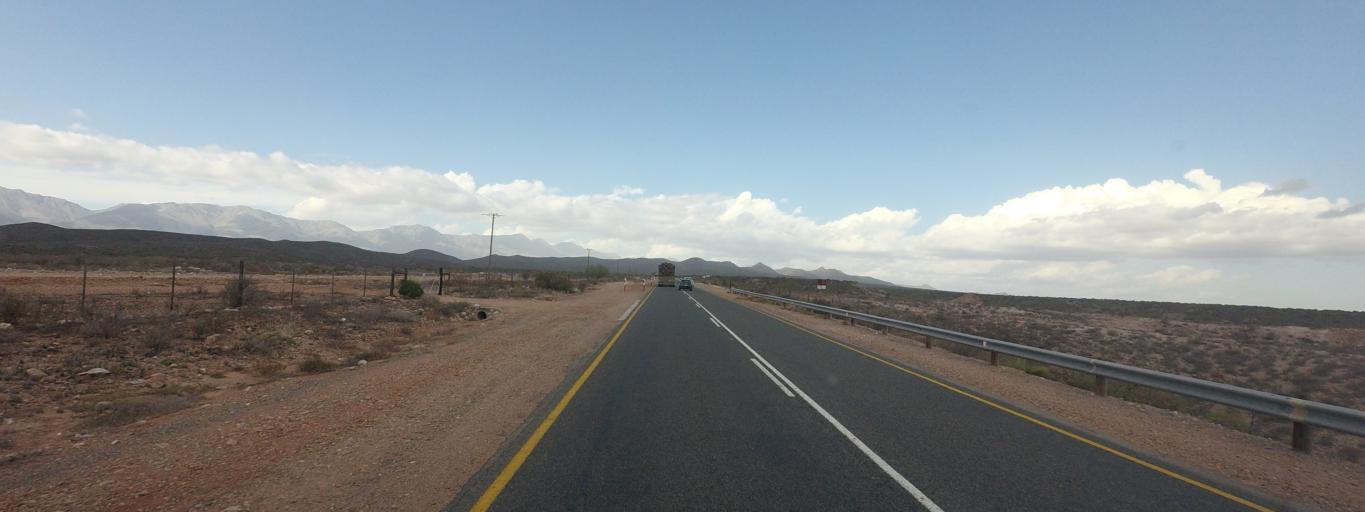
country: ZA
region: Western Cape
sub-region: Central Karoo District Municipality
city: Prince Albert
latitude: -33.5298
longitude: 21.7153
